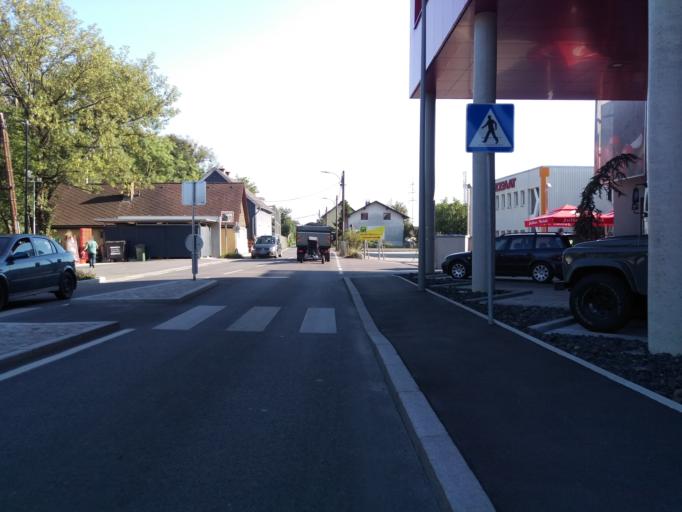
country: AT
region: Styria
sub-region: Politischer Bezirk Graz-Umgebung
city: Feldkirchen bei Graz
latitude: 47.0381
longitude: 15.4394
